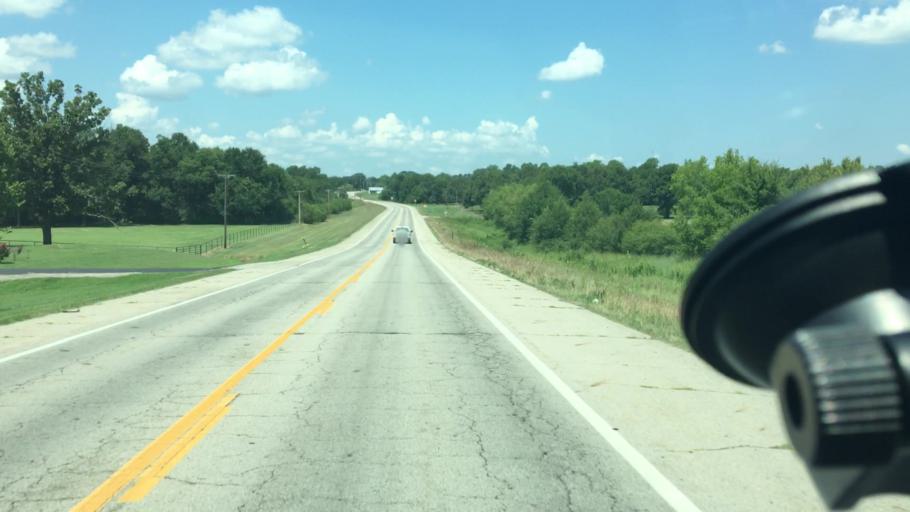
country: US
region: Arkansas
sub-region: Sebastian County
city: Lavaca
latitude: 35.2921
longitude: -94.1263
